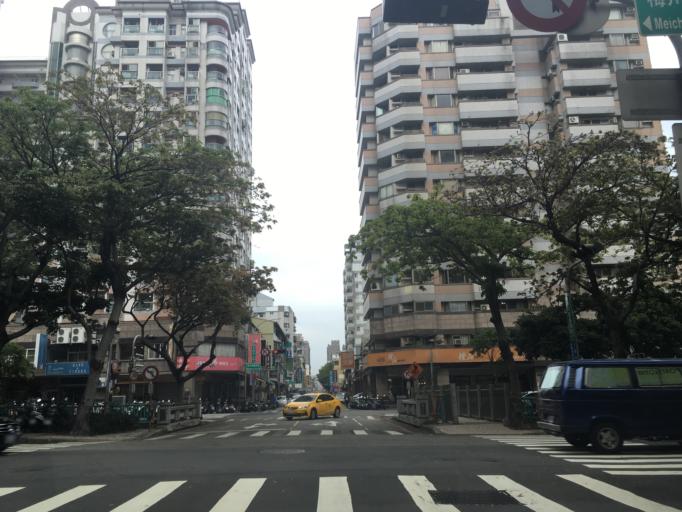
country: TW
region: Taiwan
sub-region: Taichung City
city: Taichung
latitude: 24.1741
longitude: 120.6794
